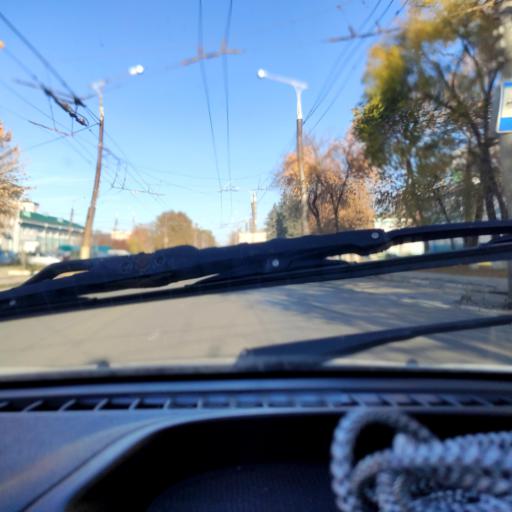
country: RU
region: Samara
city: Tol'yatti
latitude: 53.5401
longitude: 49.4431
